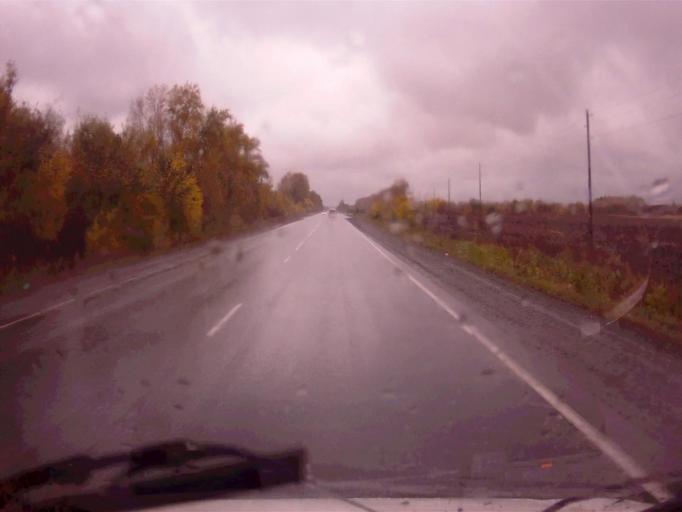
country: RU
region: Chelyabinsk
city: Argayash
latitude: 55.4327
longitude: 60.9848
